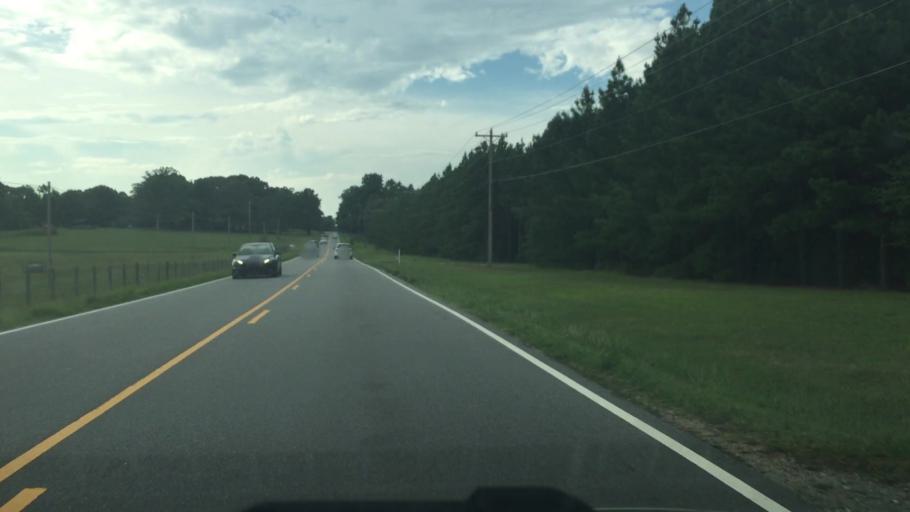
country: US
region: North Carolina
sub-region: Rowan County
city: Enochville
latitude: 35.4661
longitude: -80.7407
